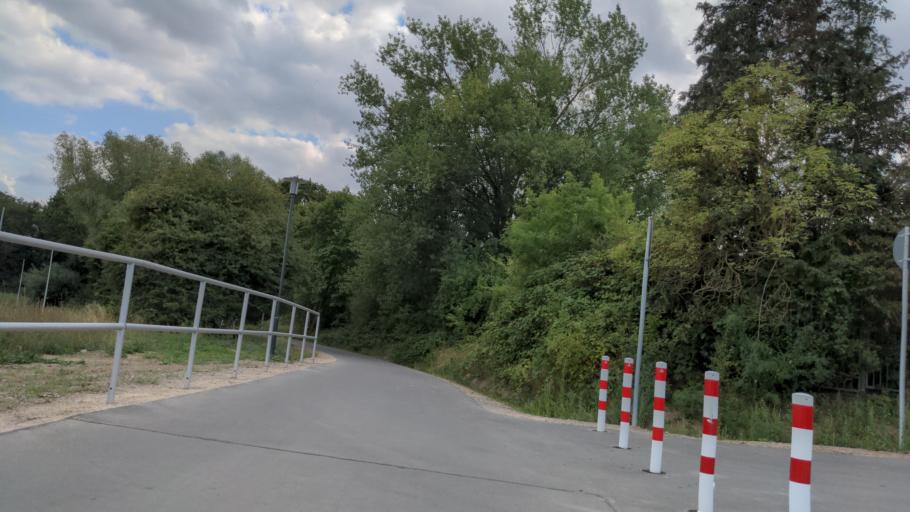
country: DE
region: Mecklenburg-Vorpommern
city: Wismar
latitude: 53.8965
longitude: 11.4328
